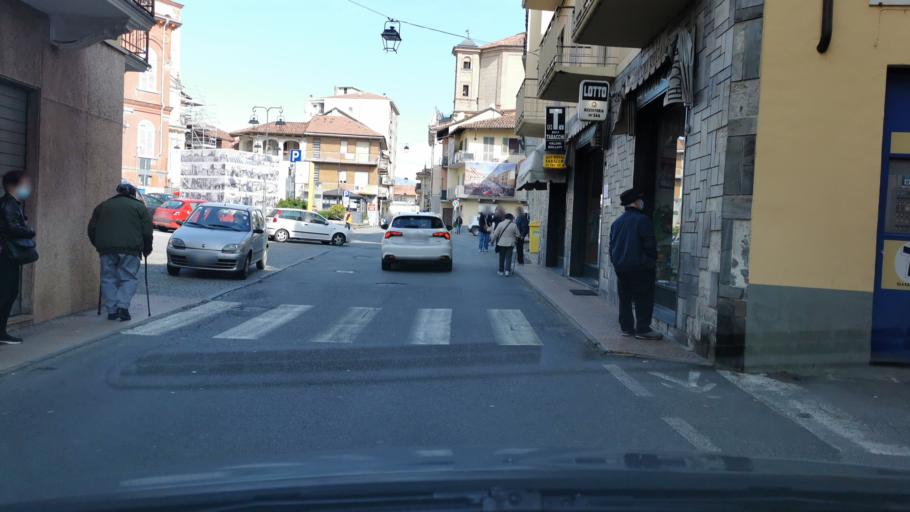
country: IT
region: Piedmont
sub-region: Provincia di Torino
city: Favria
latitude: 45.3315
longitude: 7.6909
